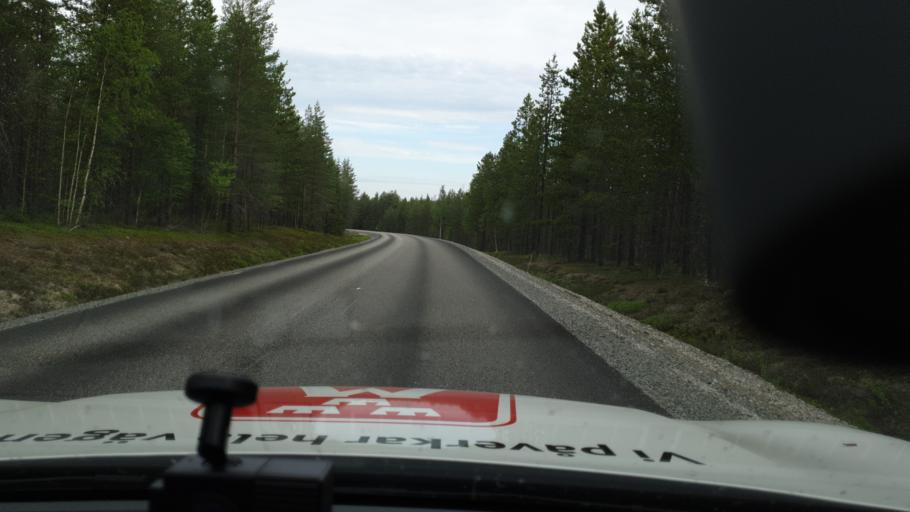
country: SE
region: Vaesterbotten
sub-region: Lycksele Kommun
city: Lycksele
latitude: 64.8870
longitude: 18.7308
